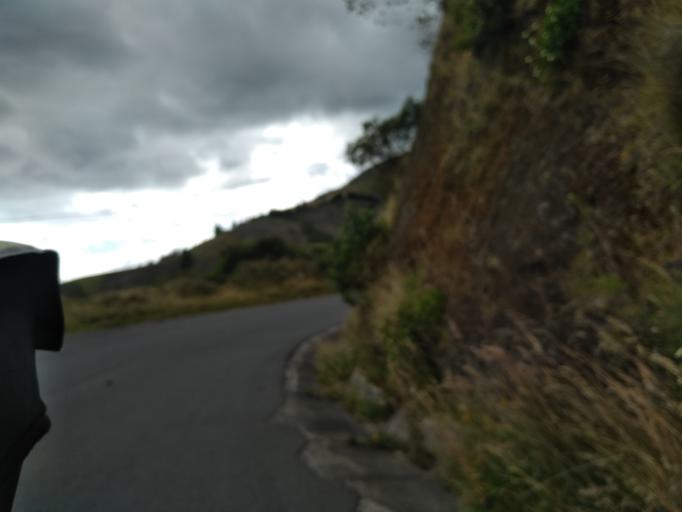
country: EC
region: Cotopaxi
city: Saquisili
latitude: -0.7266
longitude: -78.7544
